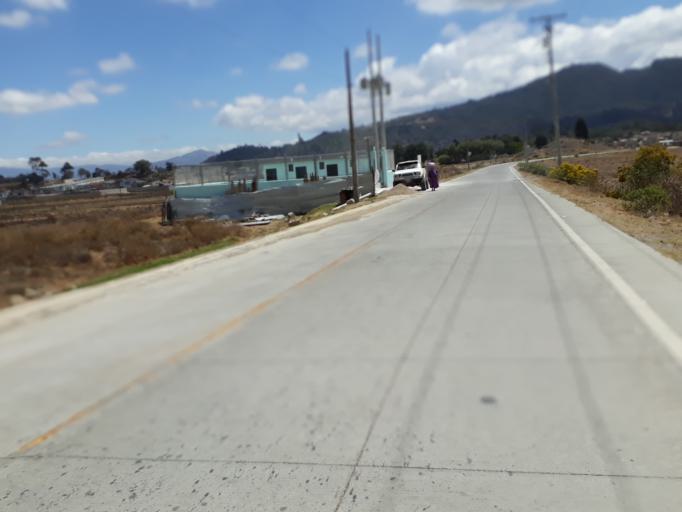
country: GT
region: Quetzaltenango
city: Quetzaltenango
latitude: 14.8155
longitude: -91.5542
